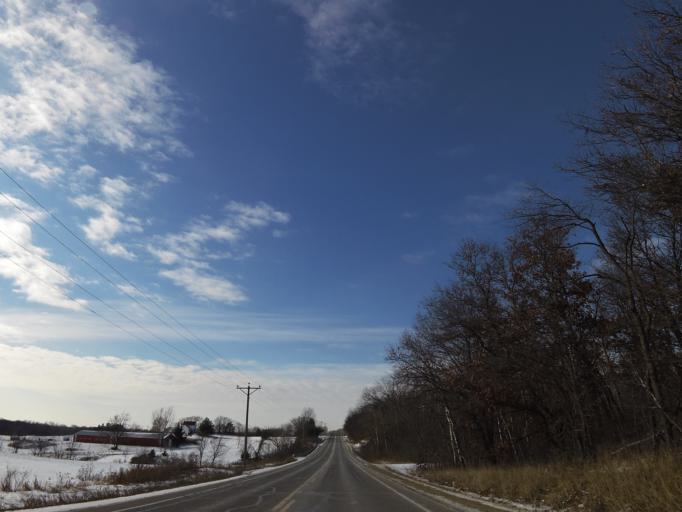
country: US
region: Wisconsin
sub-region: Saint Croix County
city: Roberts
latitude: 44.9926
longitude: -92.6005
